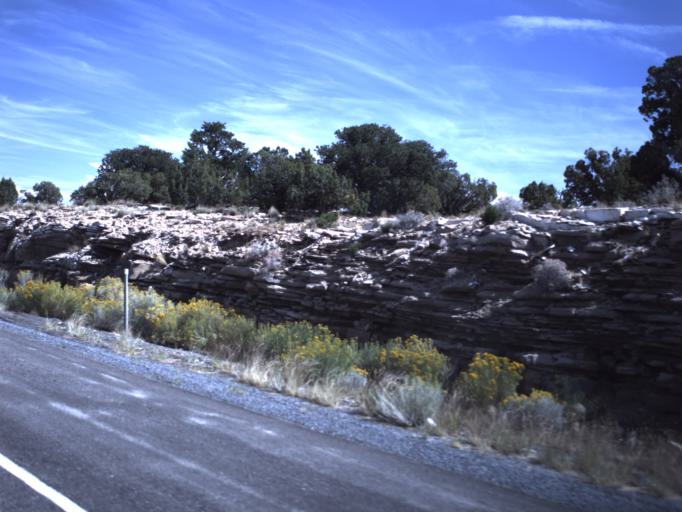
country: US
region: Utah
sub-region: Emery County
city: Castle Dale
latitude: 38.8976
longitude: -110.5802
